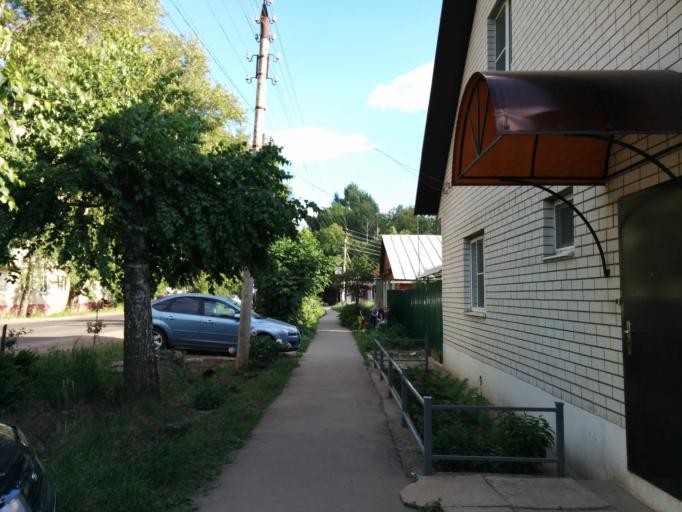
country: RU
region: Tambov
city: Tambov
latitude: 52.7490
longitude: 41.4407
